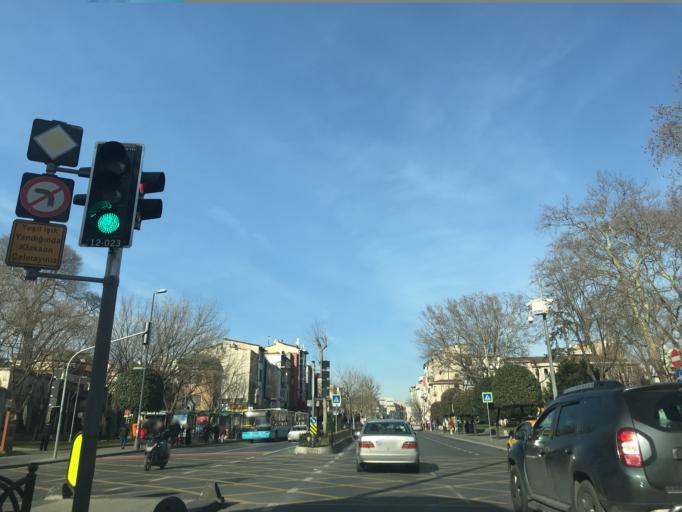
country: TR
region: Istanbul
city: Istanbul
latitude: 41.0152
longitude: 28.9534
